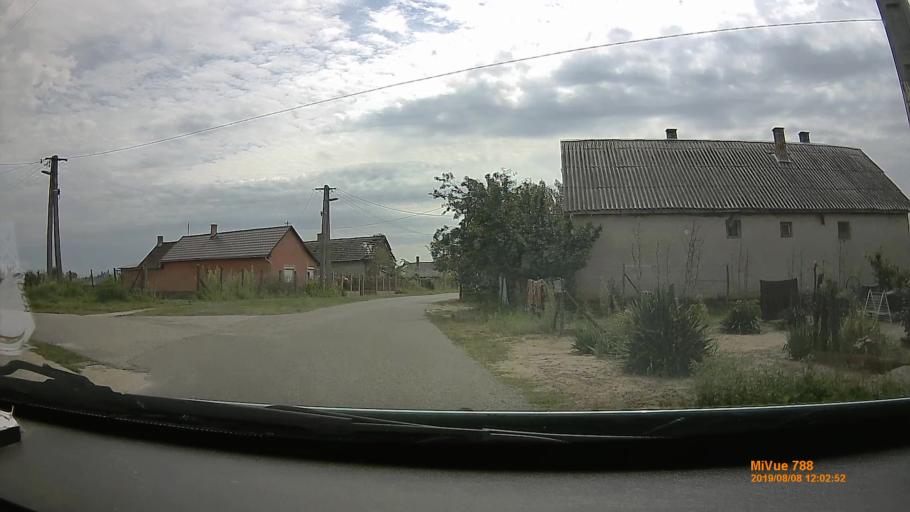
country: HU
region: Szabolcs-Szatmar-Bereg
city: Nyirbogat
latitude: 47.7929
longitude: 22.0511
